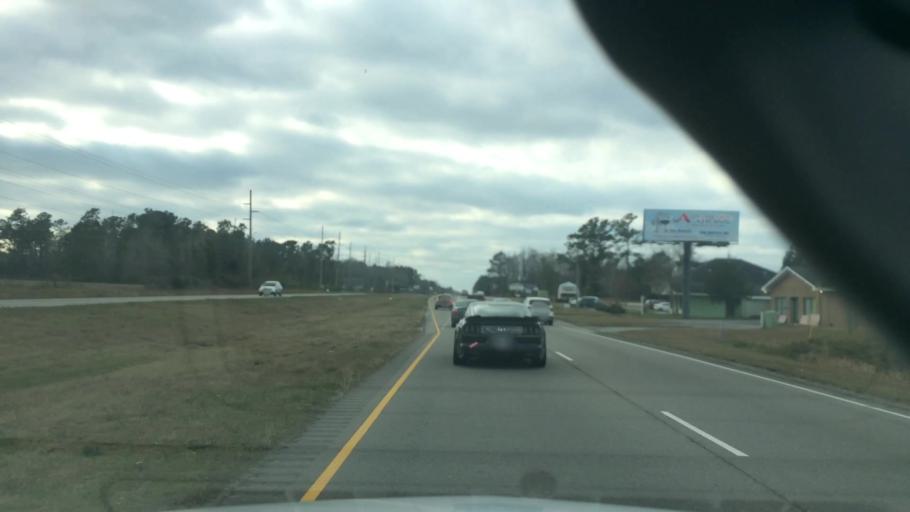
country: US
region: North Carolina
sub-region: Brunswick County
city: Shallotte
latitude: 34.0081
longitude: -78.2993
